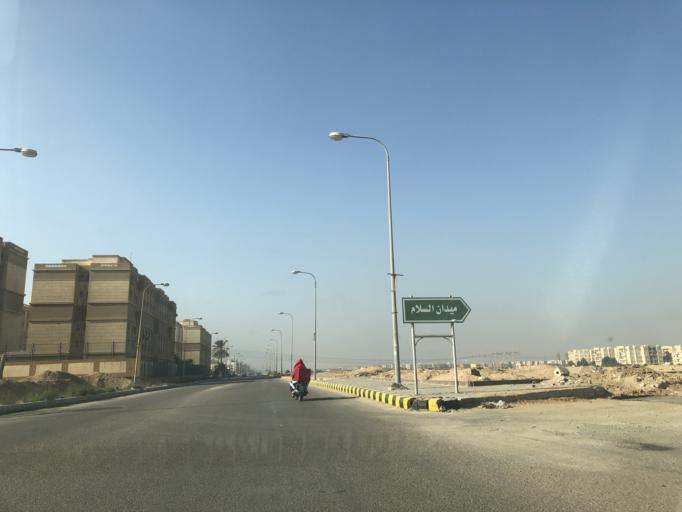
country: EG
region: Al Jizah
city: Madinat Sittah Uktubar
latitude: 29.9191
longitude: 31.0577
